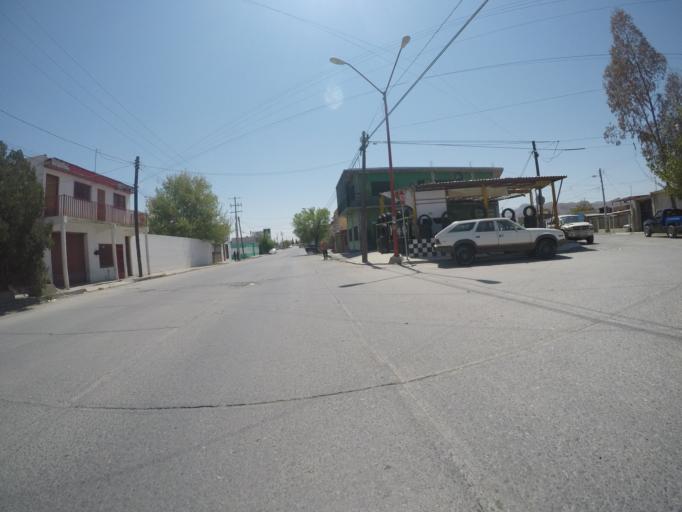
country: MX
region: Chihuahua
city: Ciudad Juarez
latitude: 31.7255
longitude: -106.4829
